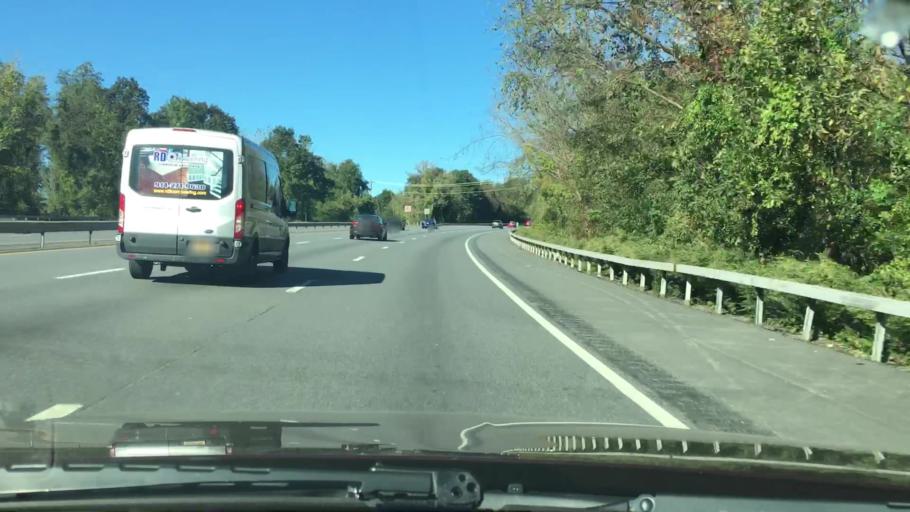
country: US
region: New York
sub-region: Westchester County
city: Heritage Hills
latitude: 41.3308
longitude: -73.6590
